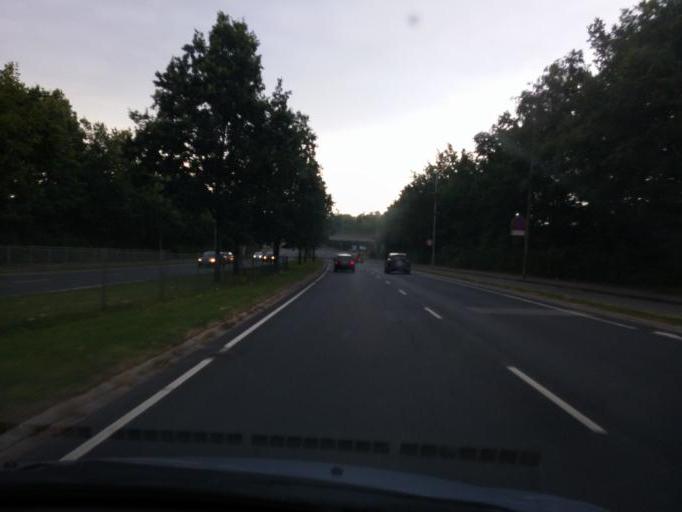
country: DK
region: South Denmark
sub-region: Odense Kommune
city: Seden
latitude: 55.3971
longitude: 10.4245
